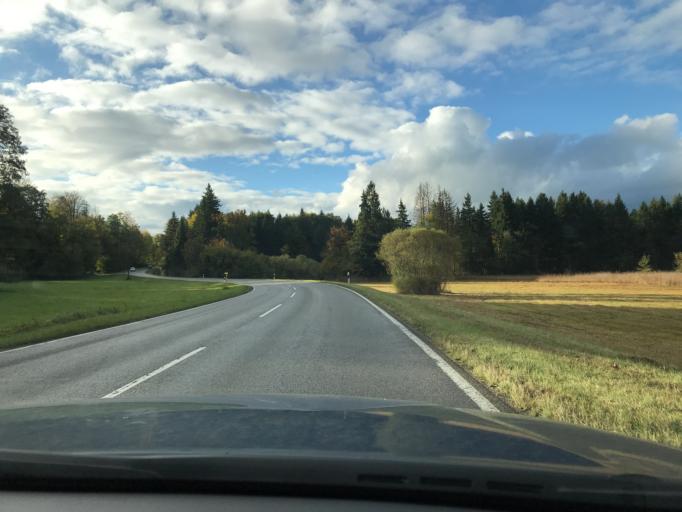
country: DE
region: Bavaria
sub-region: Upper Bavaria
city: Bad Toelz
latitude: 47.7799
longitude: 11.5550
